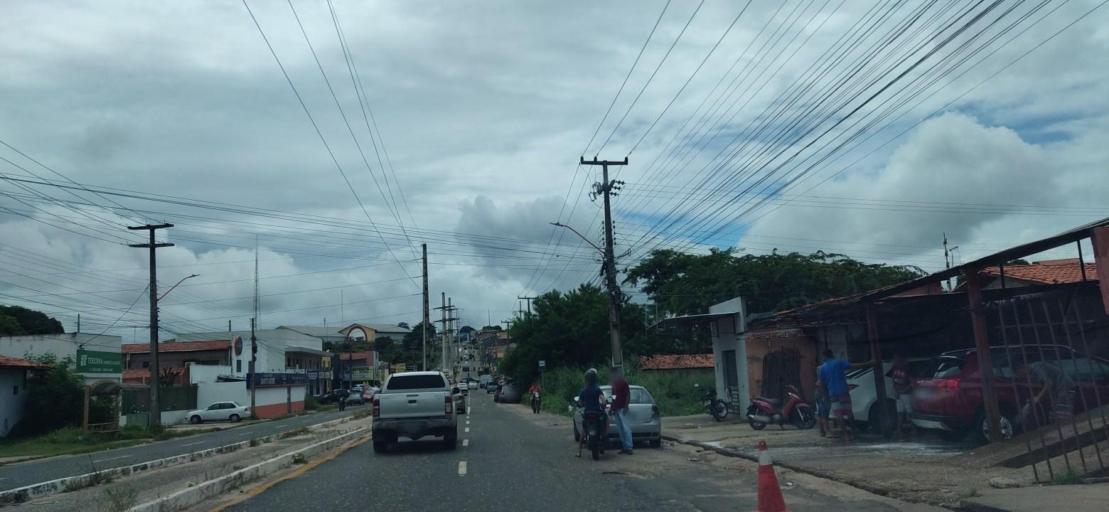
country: BR
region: Piaui
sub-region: Teresina
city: Teresina
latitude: -5.0593
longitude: -42.7533
